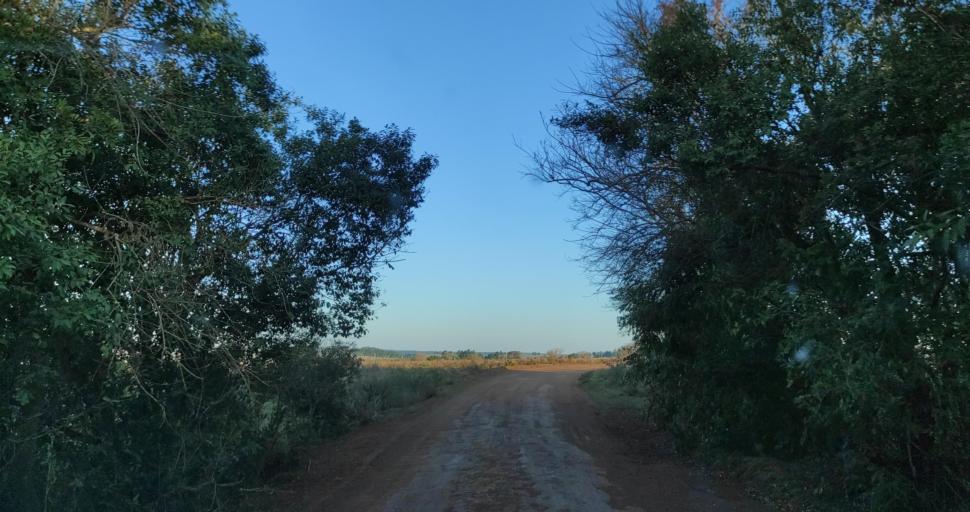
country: PY
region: Itapua
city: San Juan del Parana
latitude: -27.4381
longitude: -56.0618
